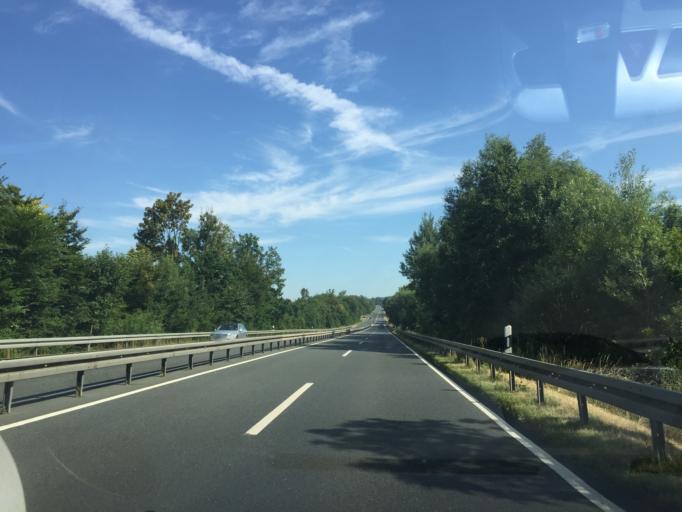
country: DE
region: Lower Saxony
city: Gittelde
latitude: 51.8125
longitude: 10.1881
